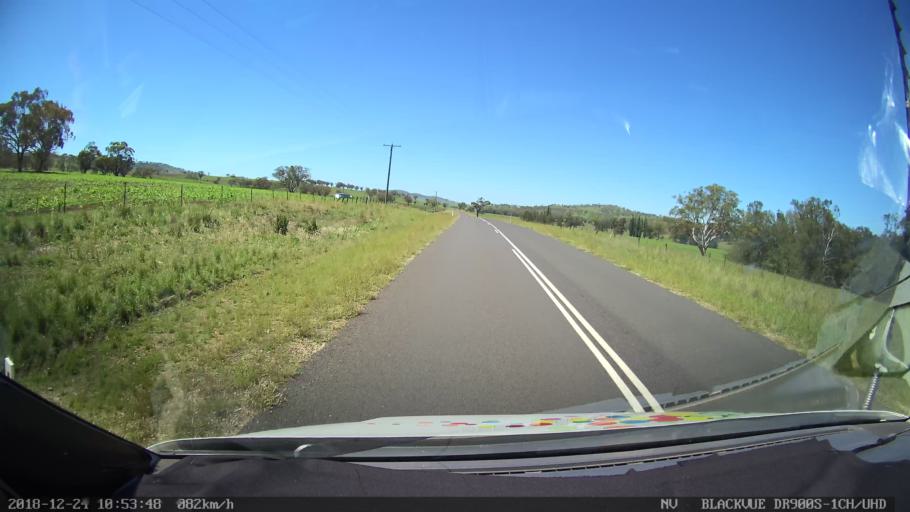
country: AU
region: New South Wales
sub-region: Upper Hunter Shire
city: Merriwa
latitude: -31.9959
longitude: 150.4192
